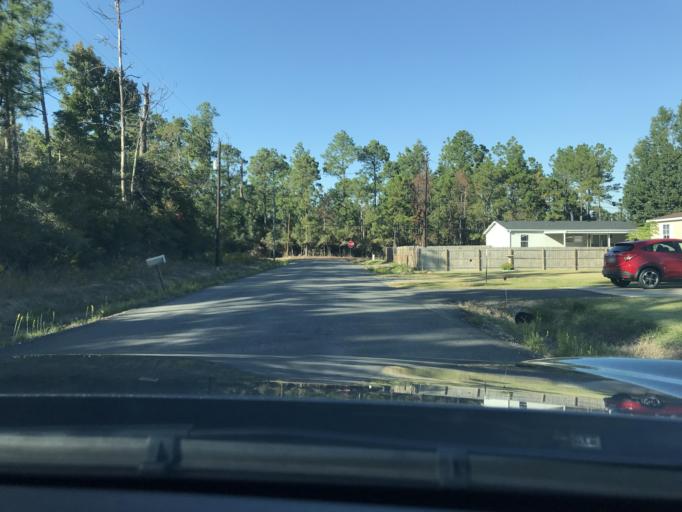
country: US
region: Louisiana
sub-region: Calcasieu Parish
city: Moss Bluff
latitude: 30.3217
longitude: -93.2688
